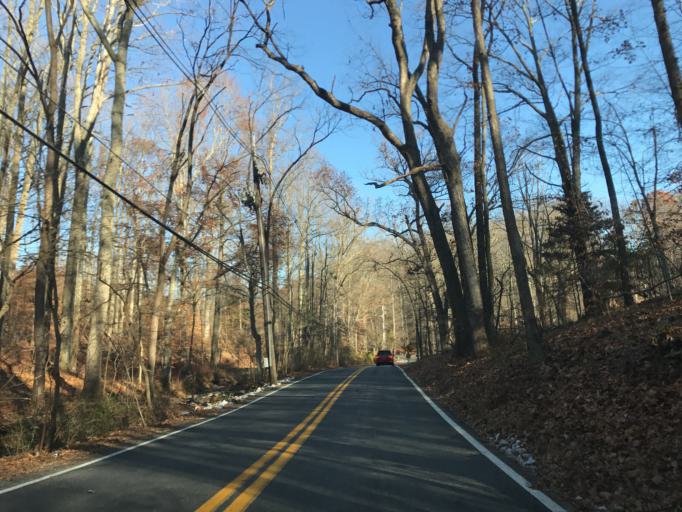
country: US
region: Maryland
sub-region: Howard County
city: Ellicott City
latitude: 39.2533
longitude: -76.7978
